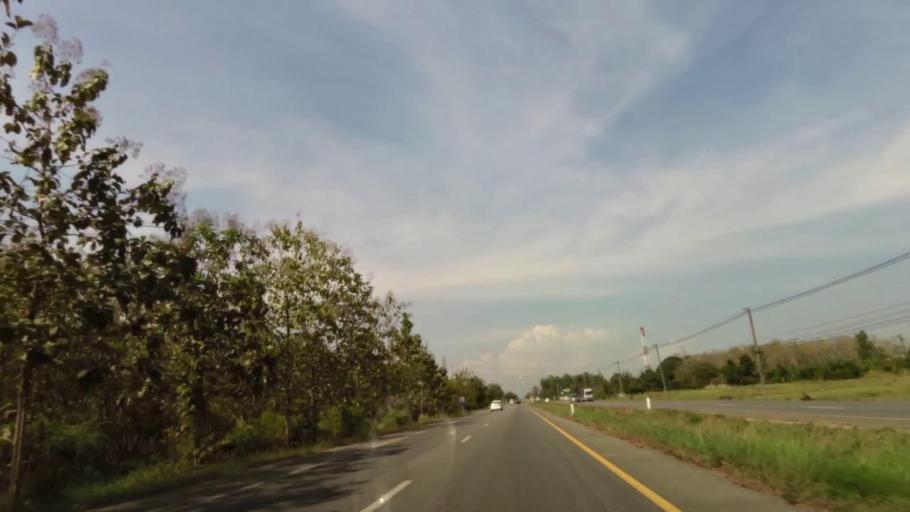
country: TH
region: Uttaradit
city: Tron
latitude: 17.5428
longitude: 100.1928
